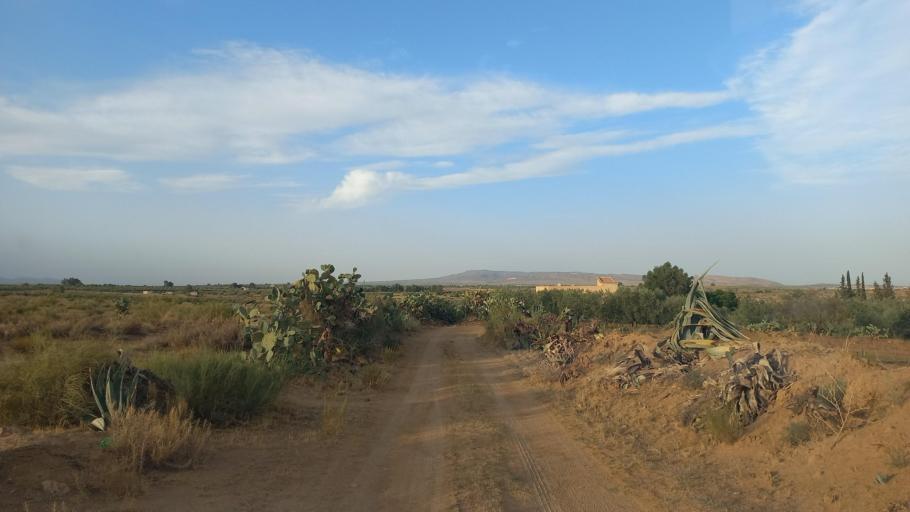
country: TN
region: Al Qasrayn
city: Kasserine
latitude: 35.2150
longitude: 9.0600
